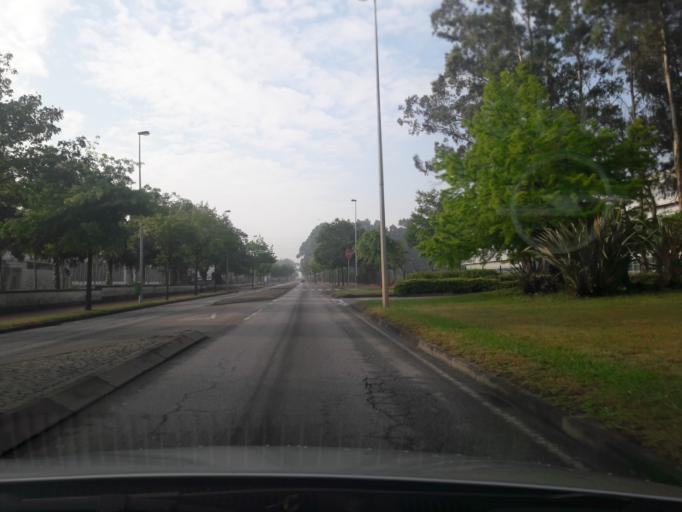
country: PT
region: Porto
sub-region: Vila do Conde
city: Arvore
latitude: 41.3255
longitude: -8.7160
